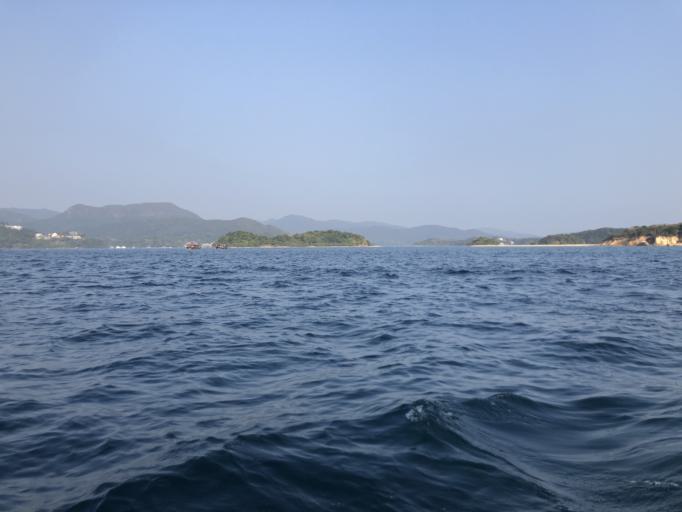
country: HK
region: Sai Kung
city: Sai Kung
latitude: 22.3756
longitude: 114.2803
